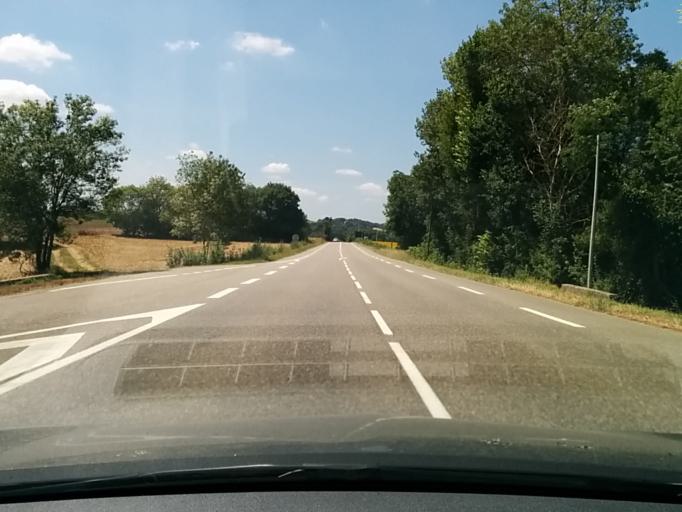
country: FR
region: Midi-Pyrenees
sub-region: Departement du Gers
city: Jegun
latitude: 43.7236
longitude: 0.3898
